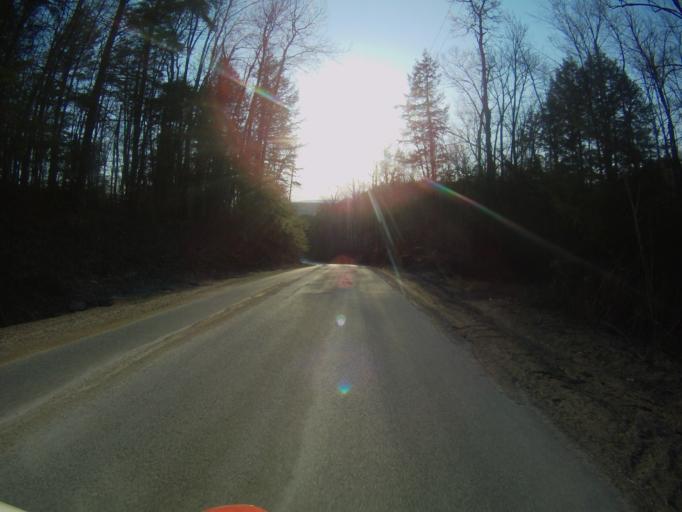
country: US
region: Vermont
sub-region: Addison County
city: Bristol
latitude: 44.0817
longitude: -73.0773
